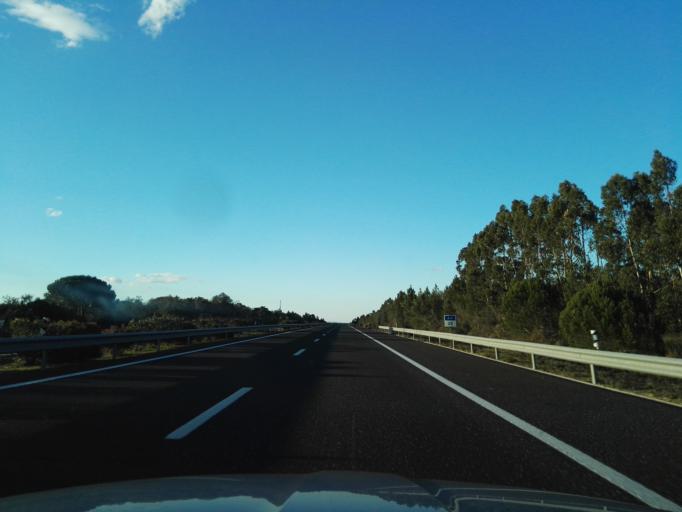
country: PT
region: Santarem
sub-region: Benavente
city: Poceirao
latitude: 38.8003
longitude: -8.6973
